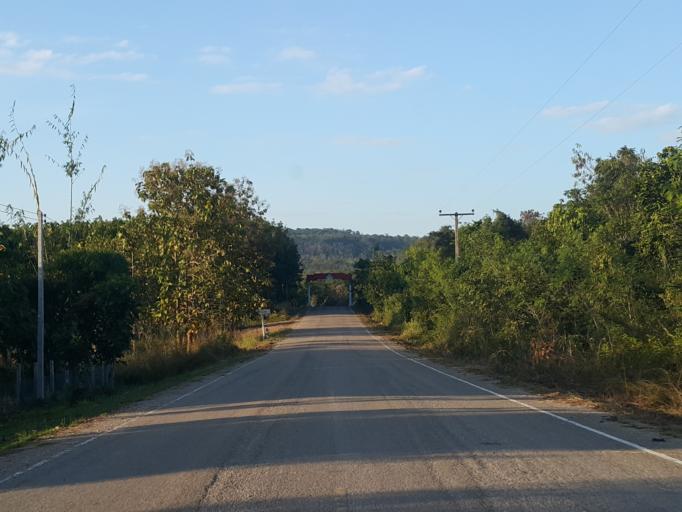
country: TH
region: Lampang
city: Lampang
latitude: 18.4353
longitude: 99.5704
